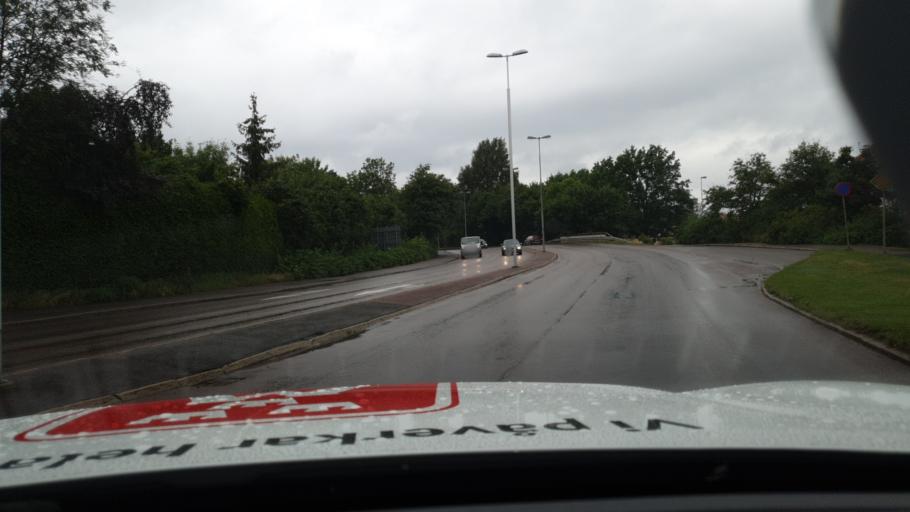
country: SE
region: Vaermland
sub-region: Kristinehamns Kommun
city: Kristinehamn
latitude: 59.3066
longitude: 14.1032
